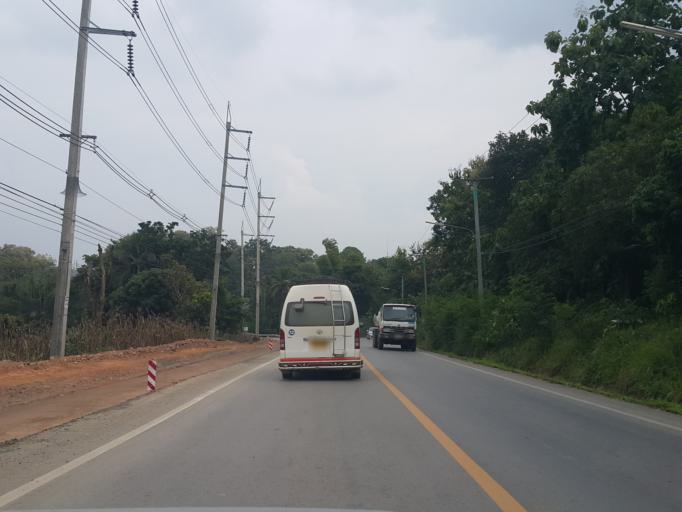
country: TH
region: Chiang Mai
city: Mae Taeng
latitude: 19.0943
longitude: 98.8773
